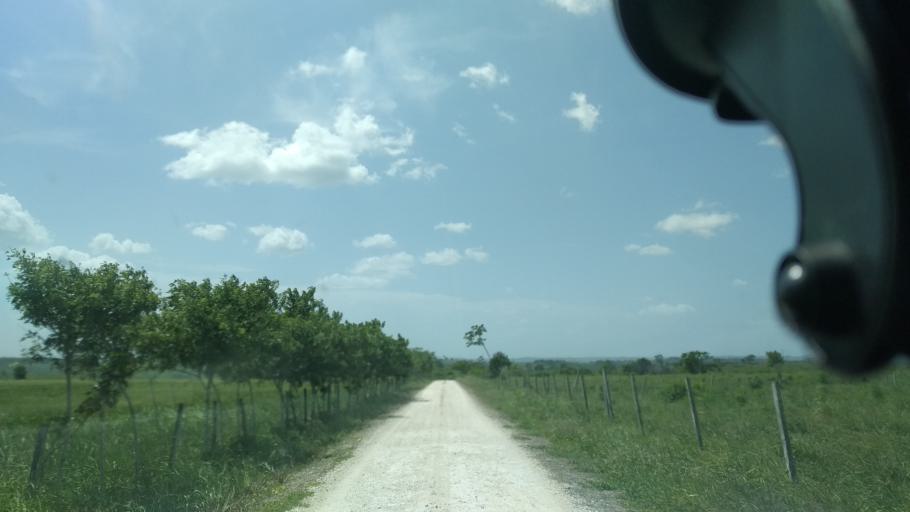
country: BZ
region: Cayo
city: San Ignacio
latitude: 17.2918
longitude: -89.0683
